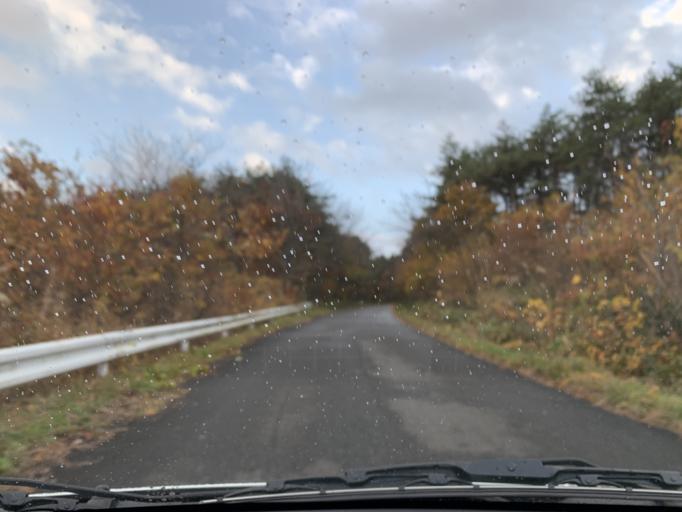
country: JP
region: Iwate
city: Mizusawa
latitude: 39.0792
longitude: 141.0233
